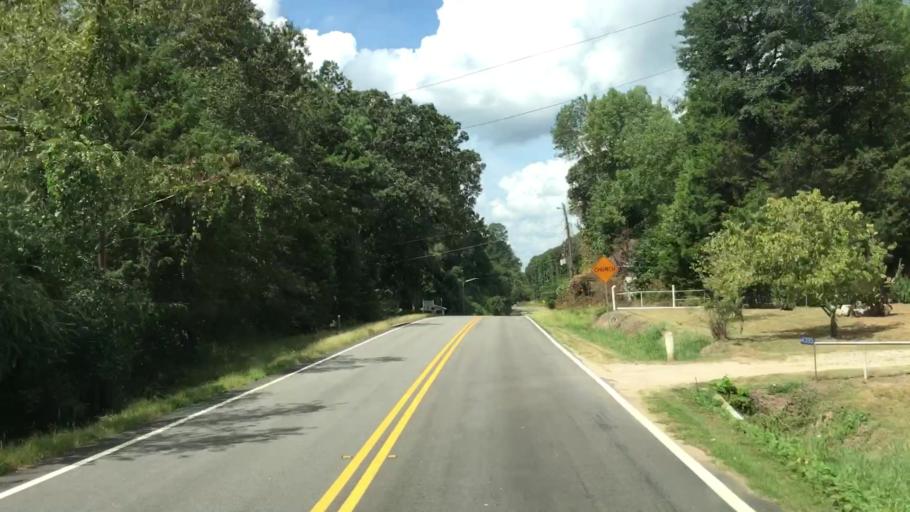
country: US
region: Georgia
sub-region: Greene County
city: Union Point
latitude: 33.5381
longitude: -83.0852
